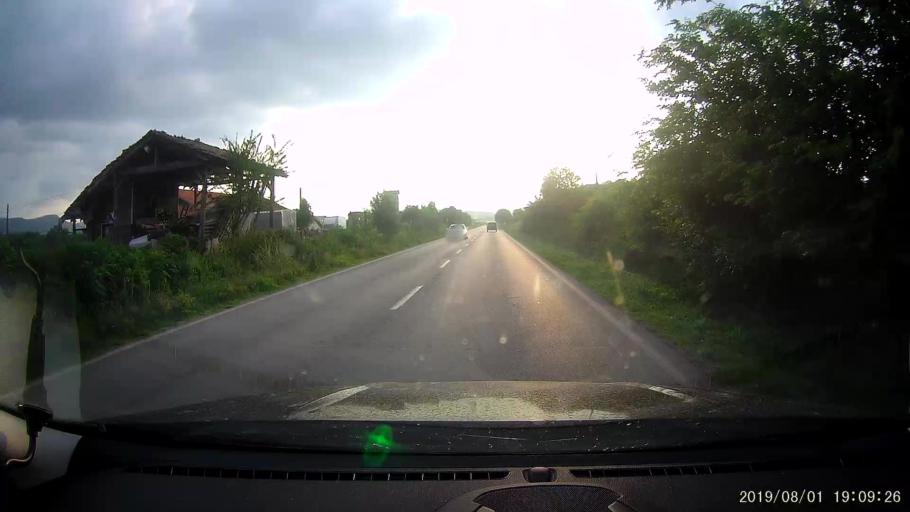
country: BG
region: Shumen
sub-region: Obshtina Smyadovo
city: Smyadovo
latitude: 42.9843
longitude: 27.0038
